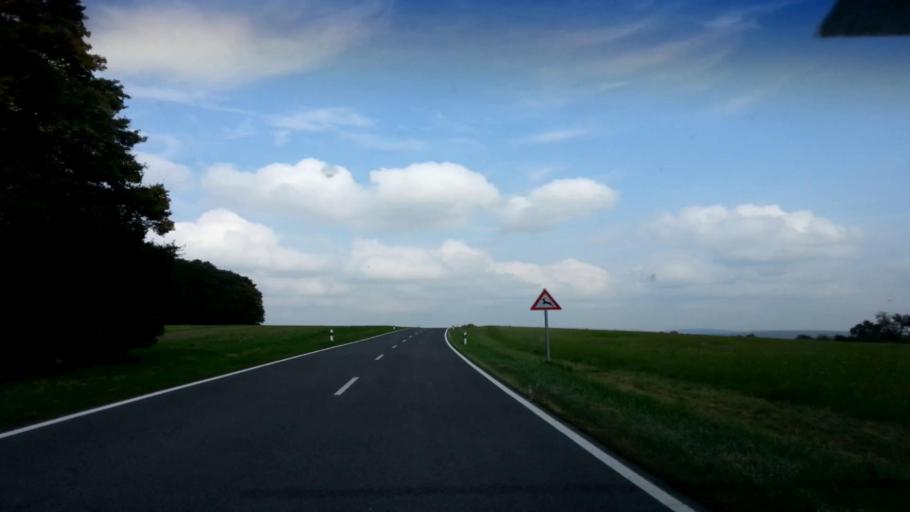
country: DE
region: Bavaria
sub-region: Regierungsbezirk Unterfranken
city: Eltmann
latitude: 49.9625
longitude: 10.6414
